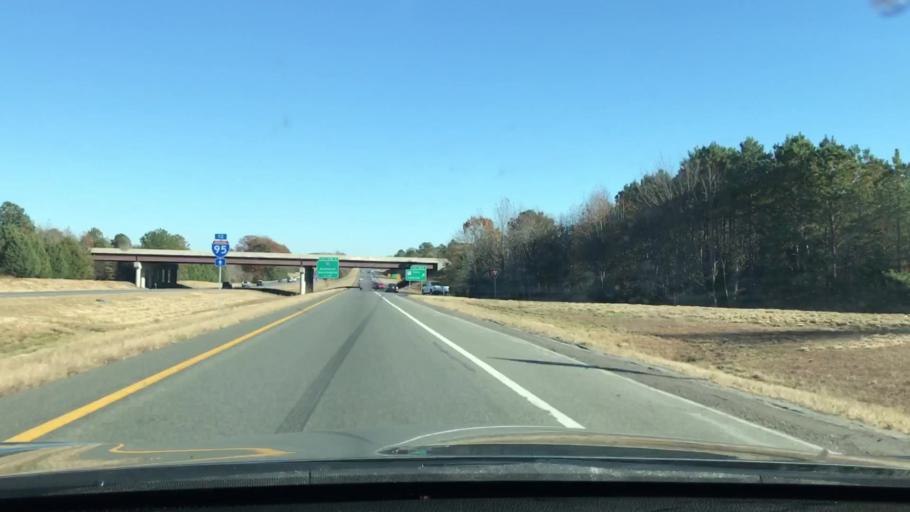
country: US
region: Virginia
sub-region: Henrico County
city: Glen Allen
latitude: 37.6585
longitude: -77.4625
